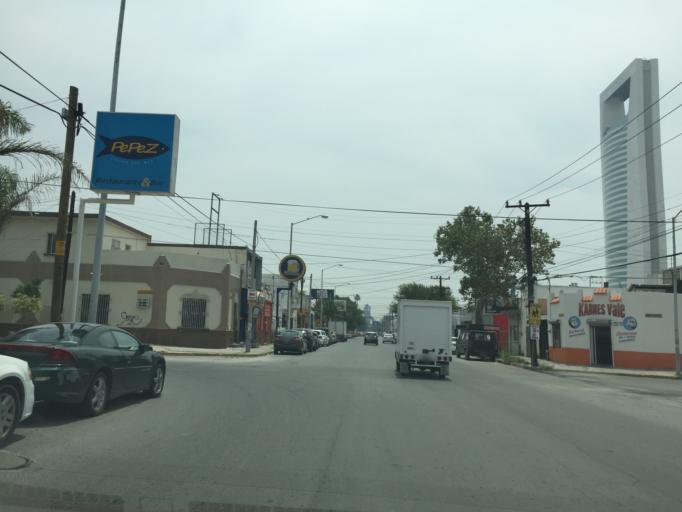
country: MX
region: Nuevo Leon
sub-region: Monterrey
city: Monterrey
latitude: 25.6777
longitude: -100.2960
